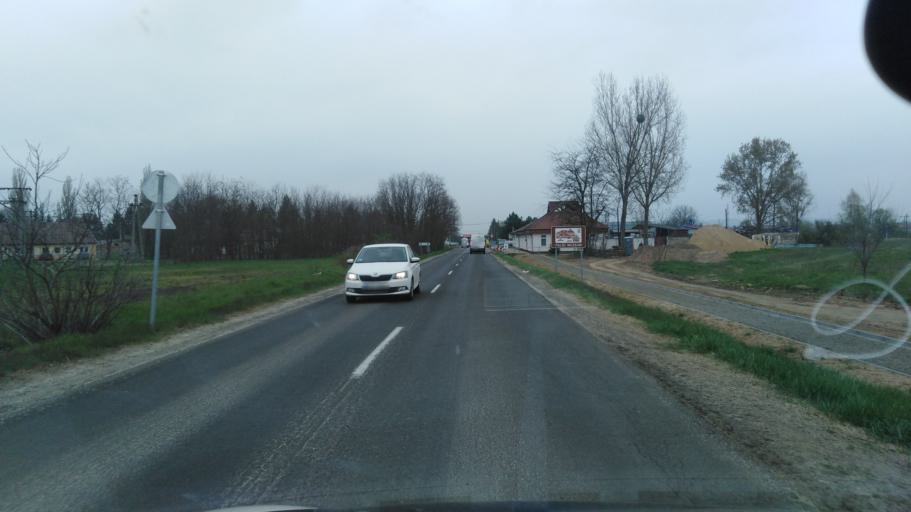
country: HU
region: Nograd
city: Balassagyarmat
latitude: 48.0597
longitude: 19.3059
